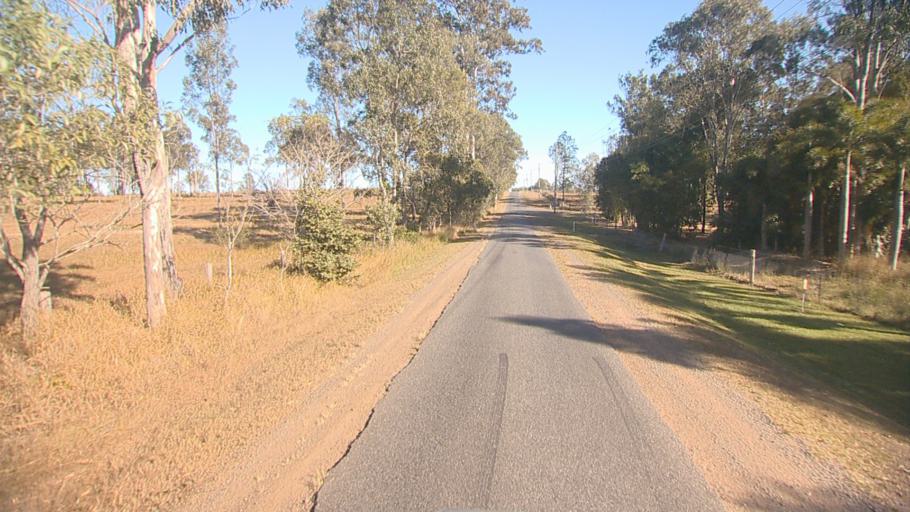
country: AU
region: Queensland
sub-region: Logan
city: Cedar Vale
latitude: -27.8474
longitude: 153.0140
